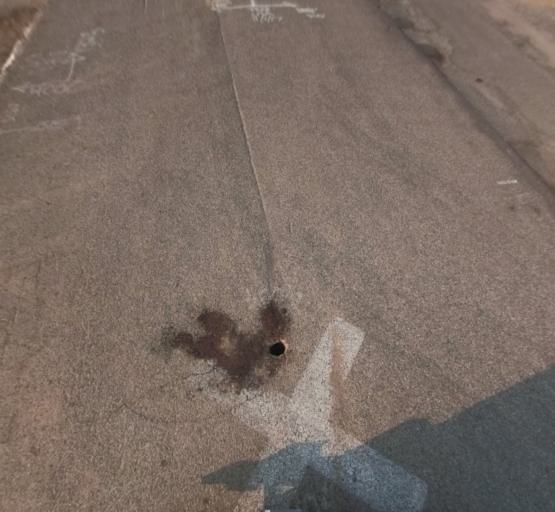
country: US
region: California
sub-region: Madera County
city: Madera Acres
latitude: 37.0108
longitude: -120.0562
